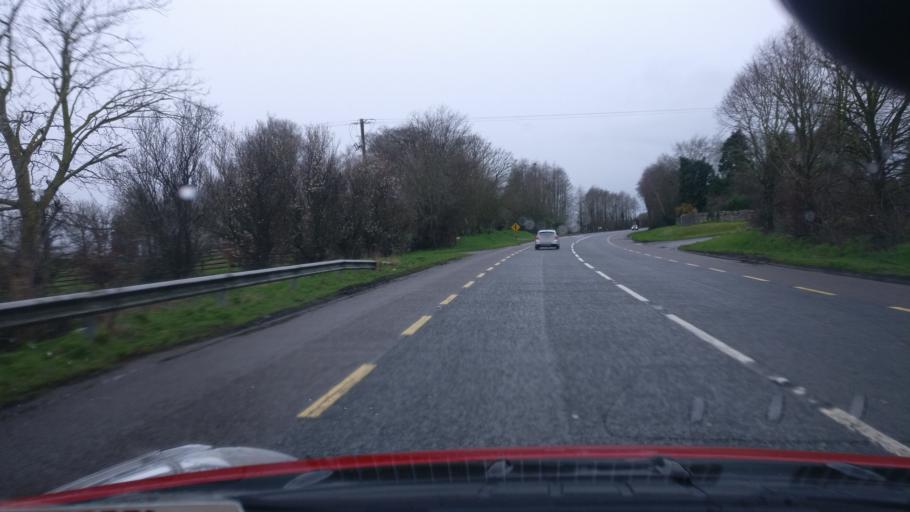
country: IE
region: Munster
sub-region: County Limerick
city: Rathkeale
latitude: 52.5285
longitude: -8.8930
